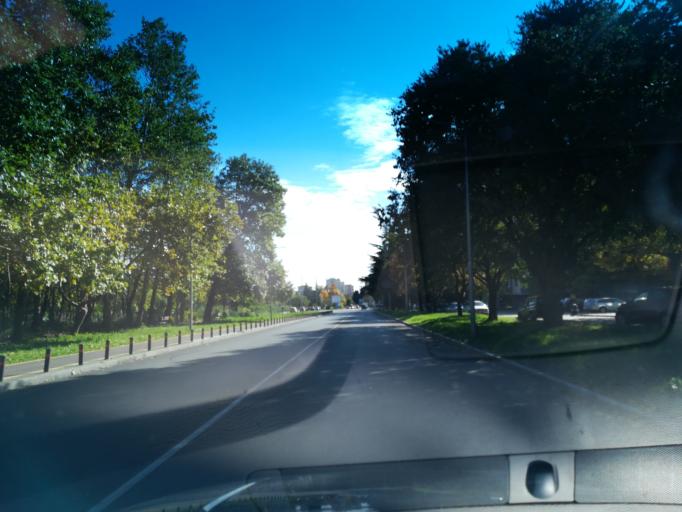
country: BG
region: Stara Zagora
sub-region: Obshtina Stara Zagora
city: Stara Zagora
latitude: 42.4358
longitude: 25.6365
